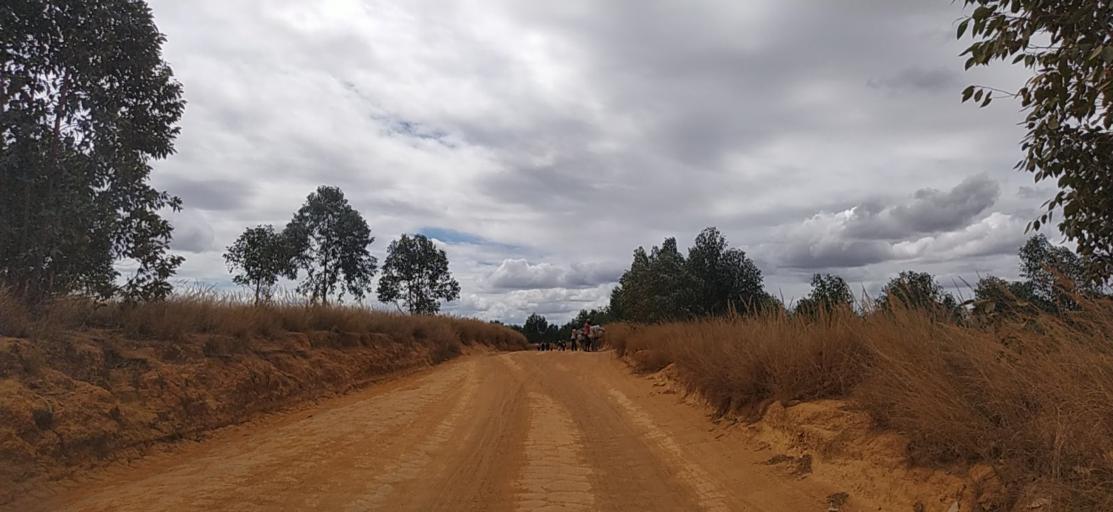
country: MG
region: Alaotra Mangoro
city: Ambatondrazaka
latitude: -17.9937
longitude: 48.2659
